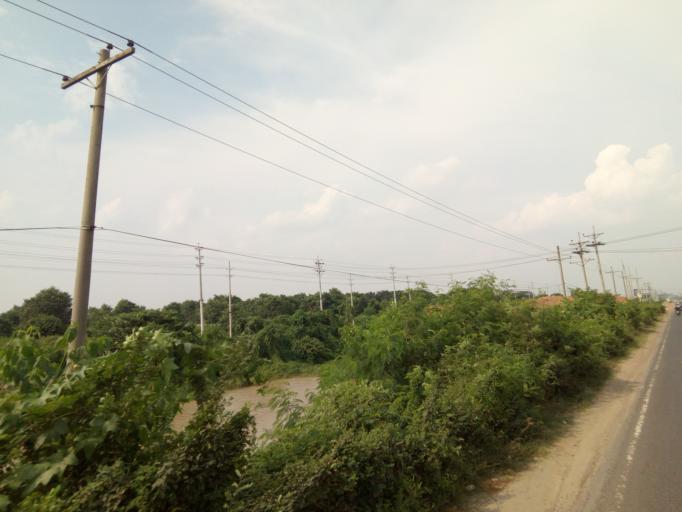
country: BD
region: Dhaka
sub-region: Dhaka
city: Dhaka
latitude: 23.6718
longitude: 90.4014
